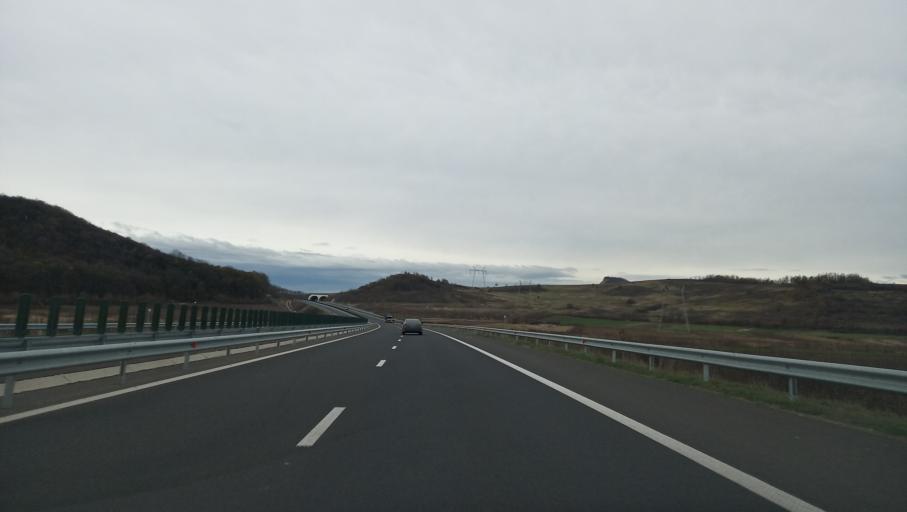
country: RO
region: Hunedoara
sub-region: Comuna Branisca
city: Branisca
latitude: 45.9361
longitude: 22.7529
